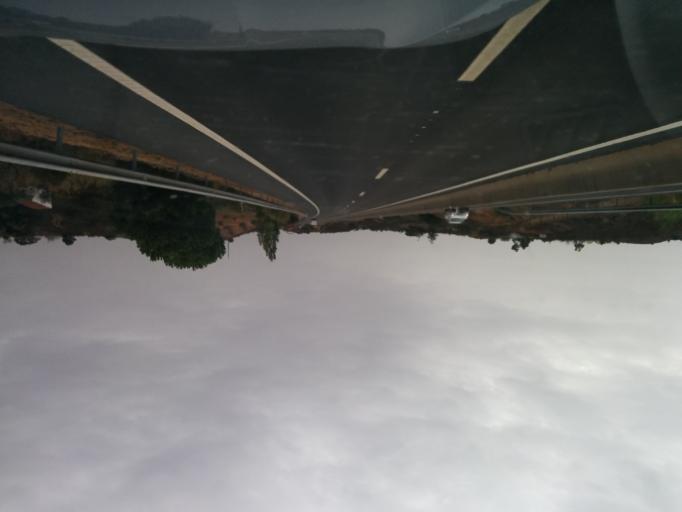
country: PT
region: Faro
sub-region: Castro Marim
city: Castro Marim
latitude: 37.2229
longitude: -7.4758
